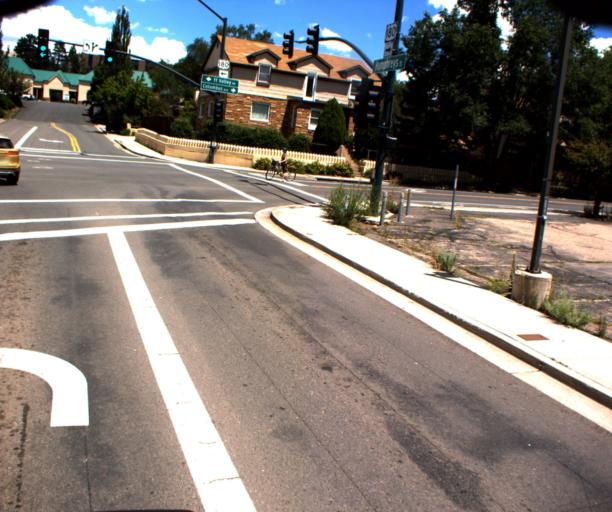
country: US
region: Arizona
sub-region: Coconino County
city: Flagstaff
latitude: 35.2063
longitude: -111.6476
